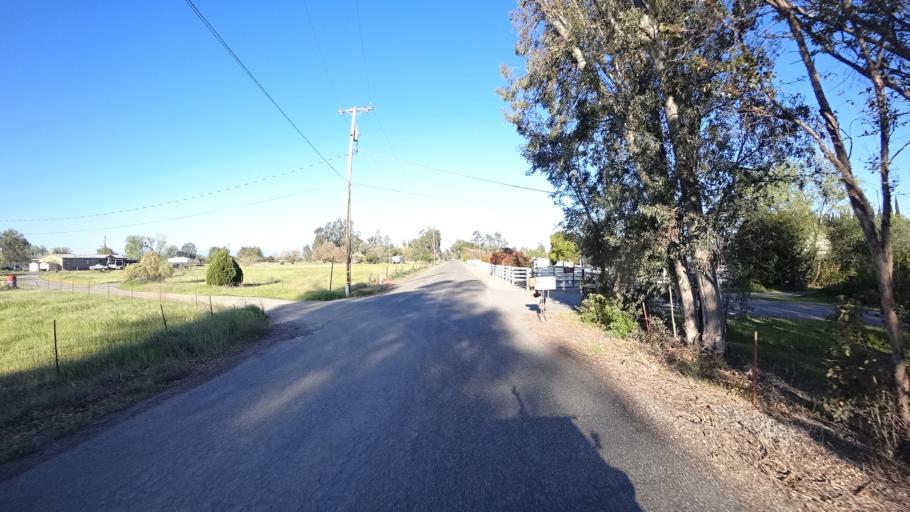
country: US
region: California
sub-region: Glenn County
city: Orland
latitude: 39.7695
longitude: -122.2221
